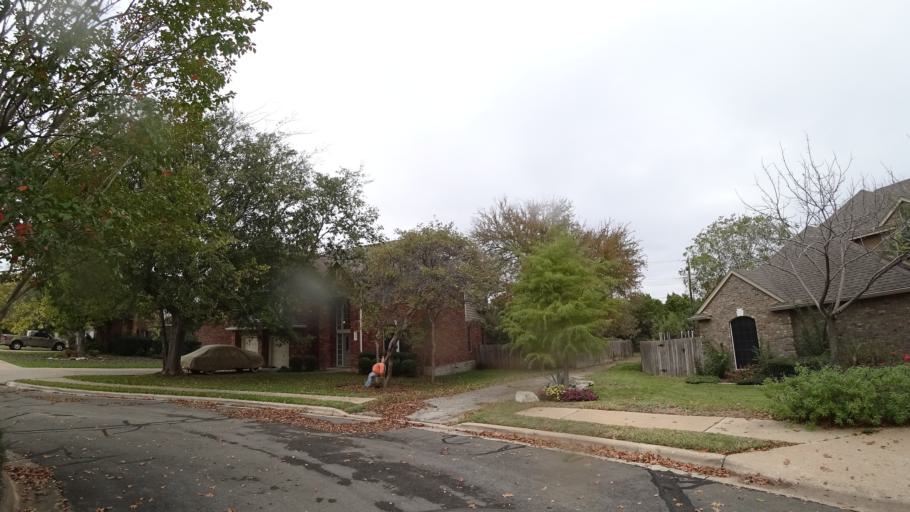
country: US
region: Texas
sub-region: Williamson County
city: Round Rock
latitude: 30.5182
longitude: -97.7047
